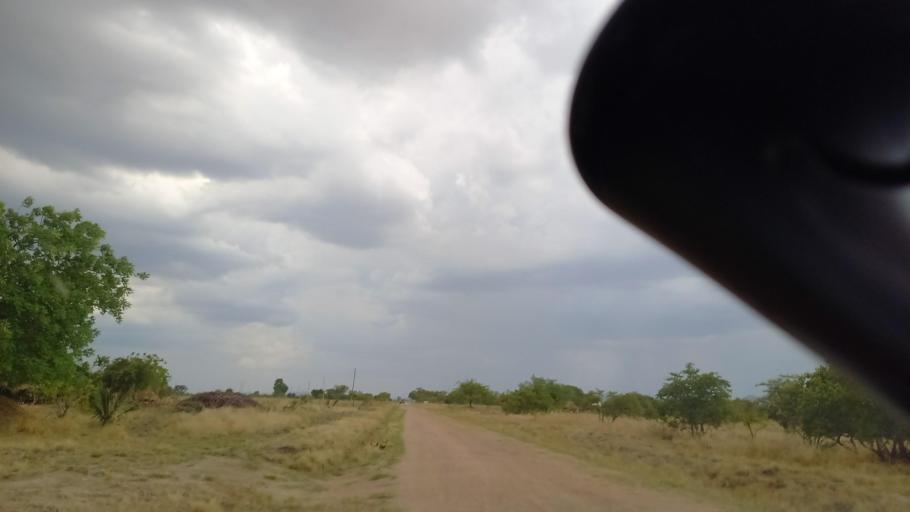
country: ZM
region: Lusaka
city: Kafue
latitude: -15.8417
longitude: 28.0915
